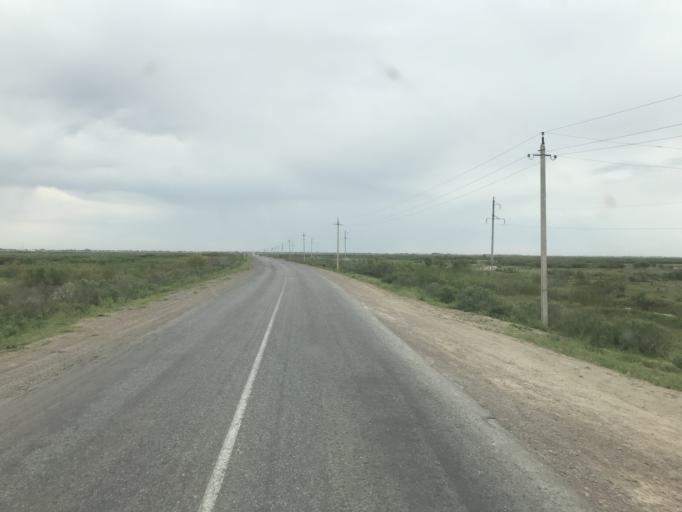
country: KZ
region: Ongtustik Qazaqstan
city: Asykata
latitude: 41.0034
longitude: 68.4712
